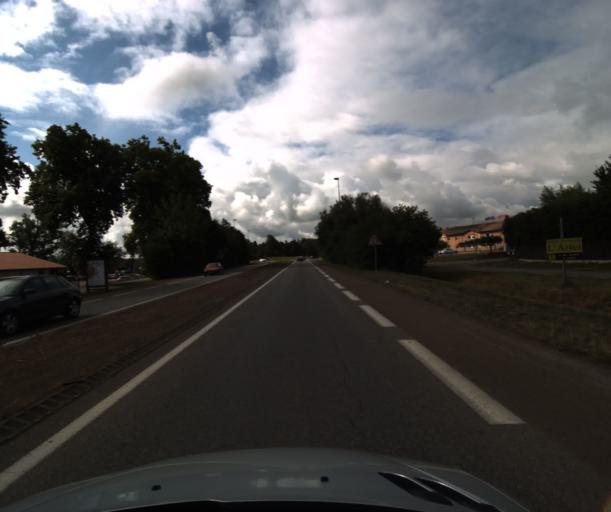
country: FR
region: Midi-Pyrenees
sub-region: Departement du Tarn-et-Garonne
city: Castelsarrasin
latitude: 44.0586
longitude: 1.0987
